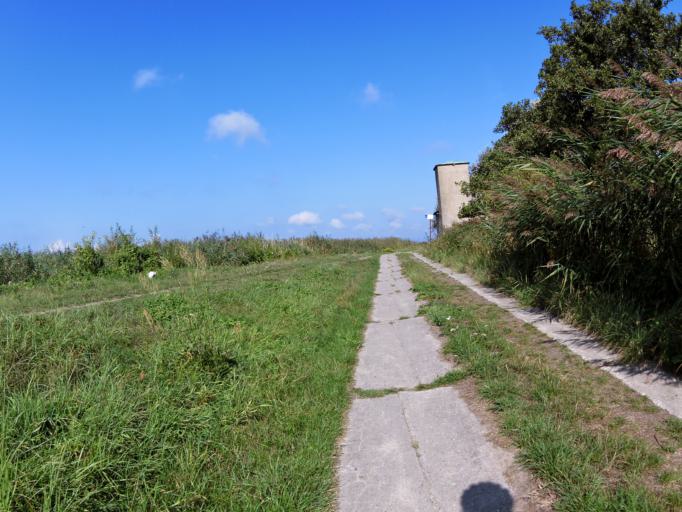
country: DE
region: Mecklenburg-Vorpommern
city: Loddin
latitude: 53.9809
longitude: 14.0491
